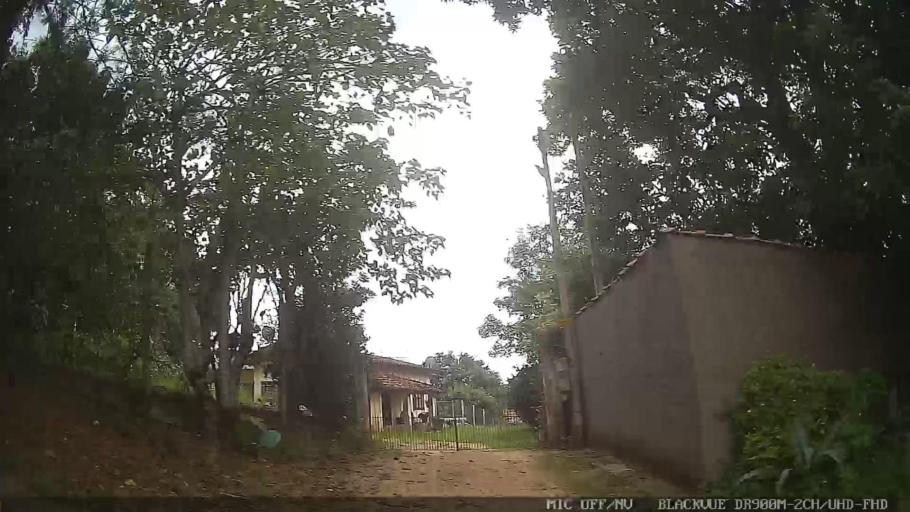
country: BR
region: Sao Paulo
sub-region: Atibaia
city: Atibaia
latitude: -23.1602
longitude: -46.5700
